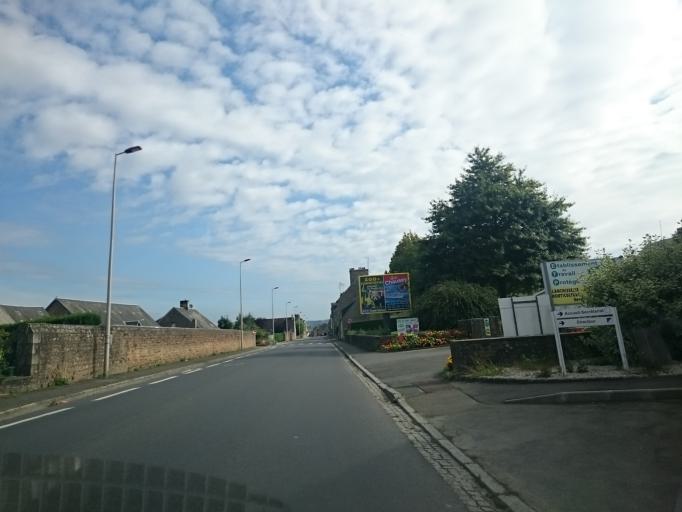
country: FR
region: Lower Normandy
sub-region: Departement de la Manche
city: Avranches
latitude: 48.6935
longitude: -1.3499
